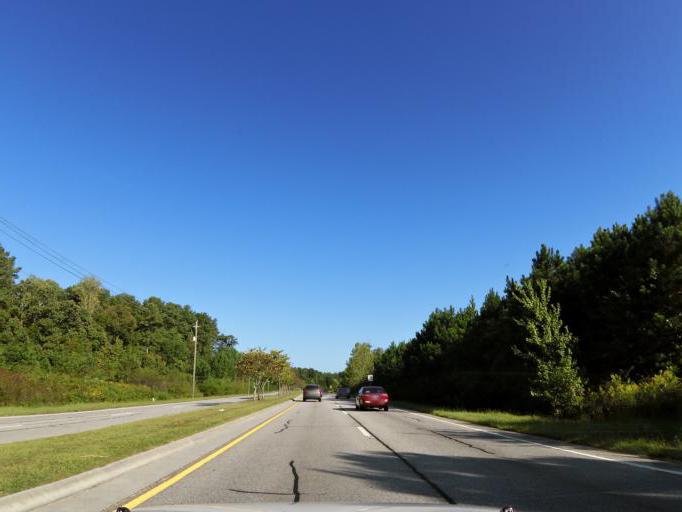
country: US
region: Georgia
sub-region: Cobb County
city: Marietta
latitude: 33.9262
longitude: -84.6306
